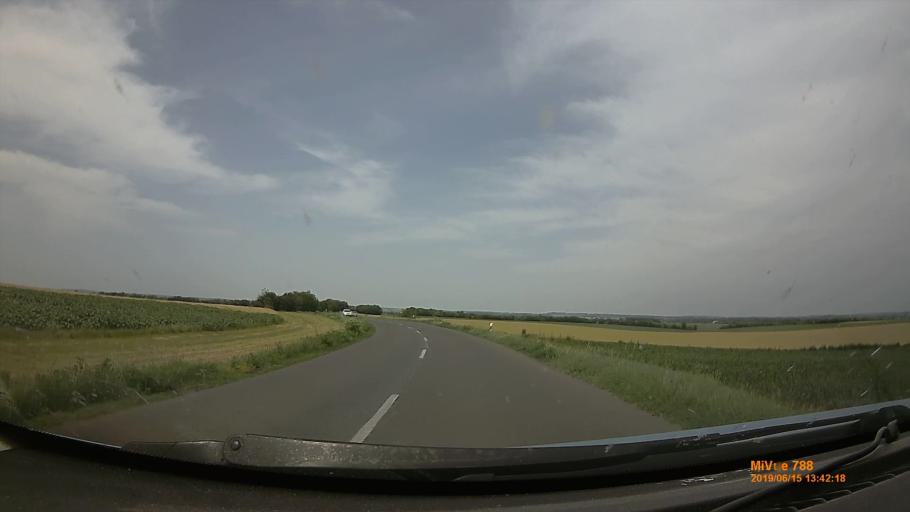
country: HU
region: Tolna
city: Iregszemcse
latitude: 46.6627
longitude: 18.1872
